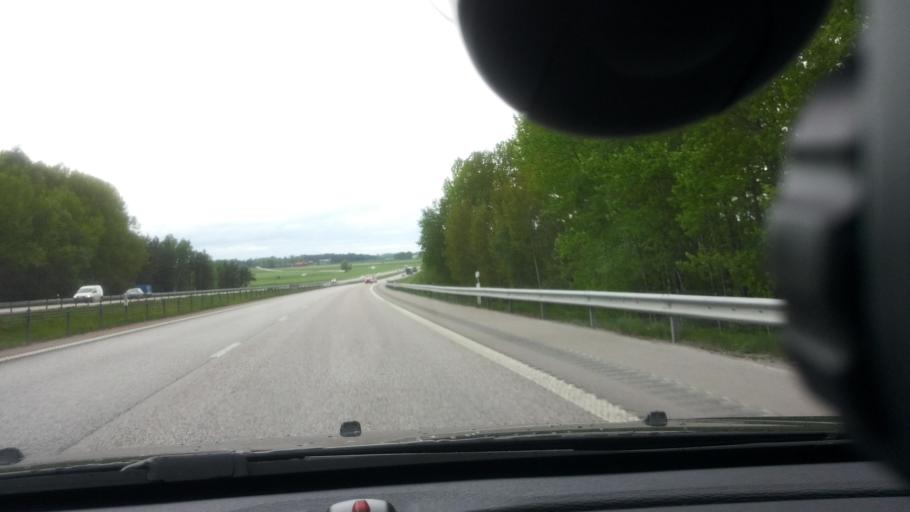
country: SE
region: Uppsala
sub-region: Uppsala Kommun
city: Alsike
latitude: 59.8031
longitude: 17.7653
